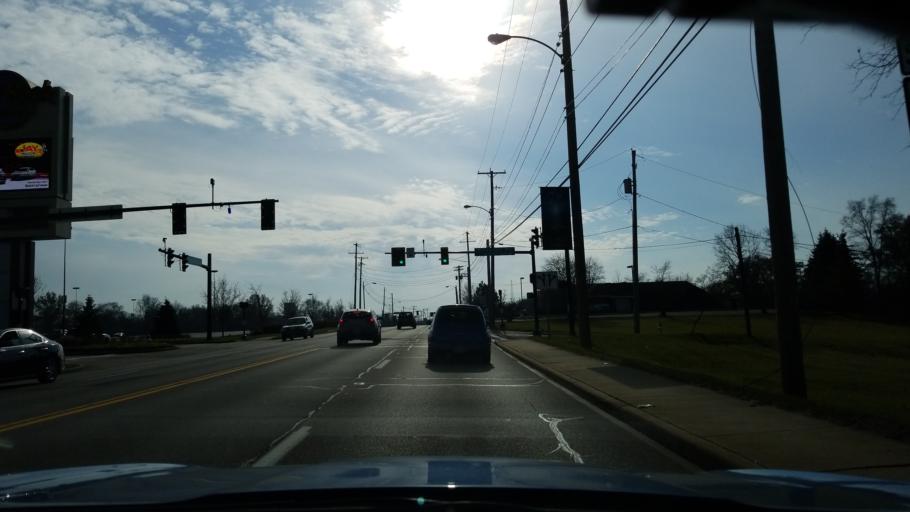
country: US
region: Ohio
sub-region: Summit County
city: Northfield
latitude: 41.3492
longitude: -81.5270
